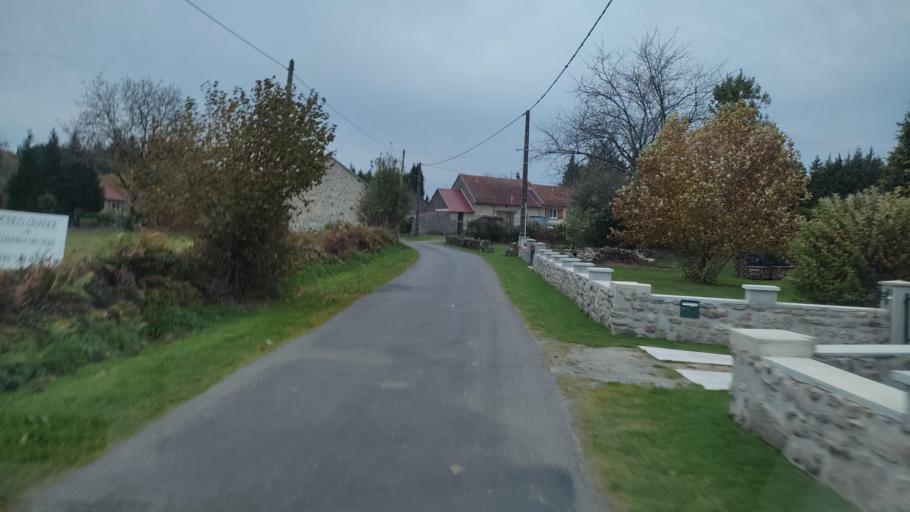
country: FR
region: Limousin
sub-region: Departement de la Haute-Vienne
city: Ambazac
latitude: 46.0322
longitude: 1.4666
